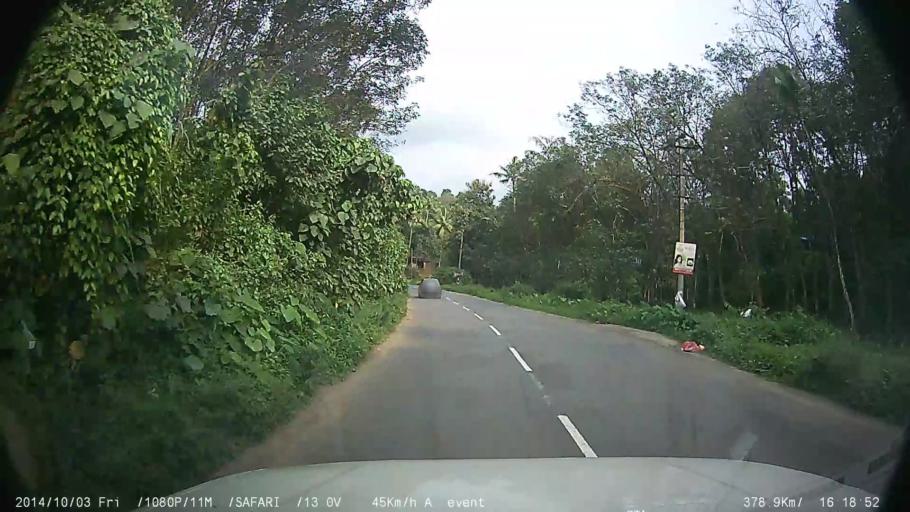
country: IN
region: Kerala
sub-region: Ernakulam
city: Muvattupuzha
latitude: 9.8970
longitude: 76.5854
